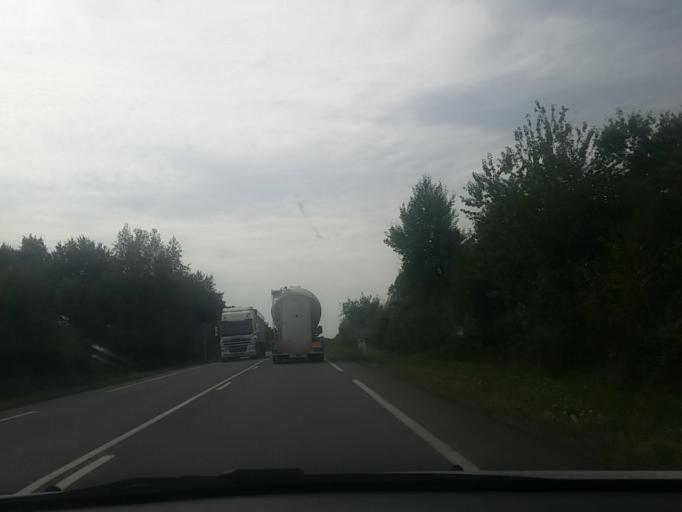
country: FR
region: Pays de la Loire
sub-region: Departement de la Vendee
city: Chantonnay
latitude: 46.6807
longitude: -1.0648
